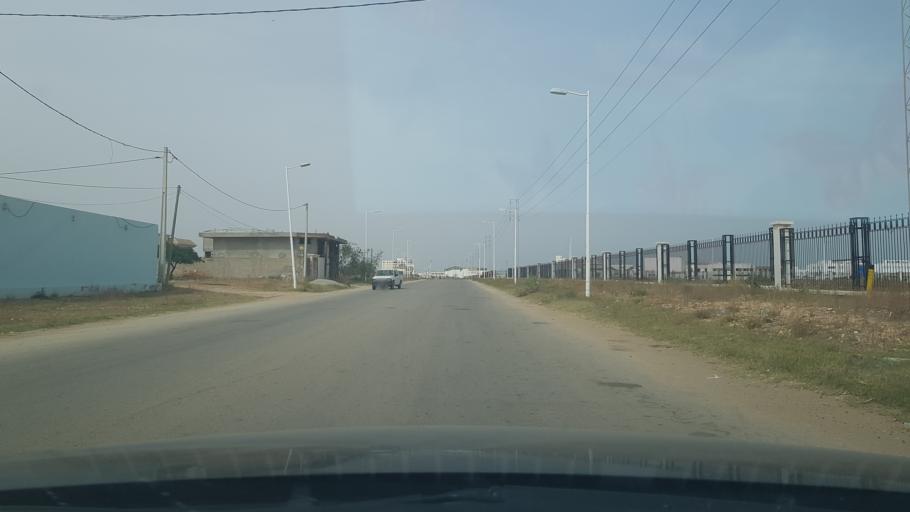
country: TN
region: Safaqis
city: Al Qarmadah
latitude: 34.8372
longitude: 10.7491
